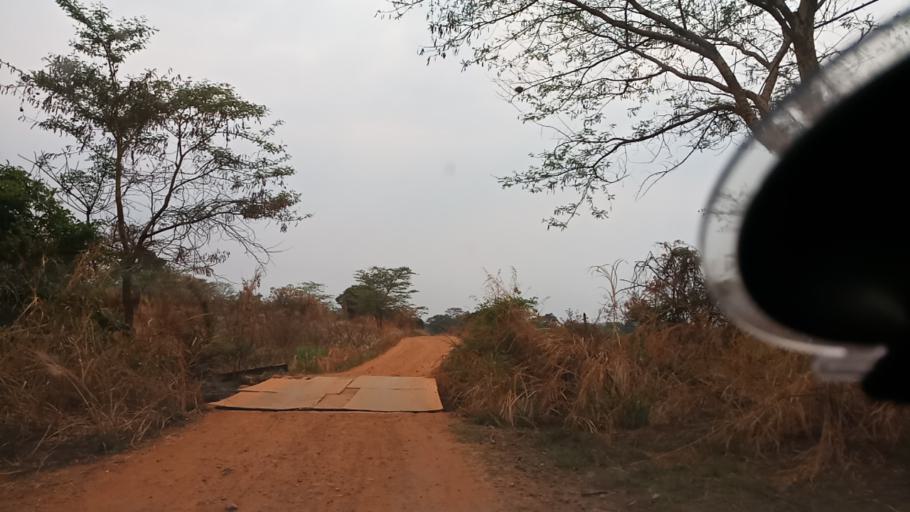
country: ZM
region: Luapula
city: Nchelenge
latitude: -9.0942
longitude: 28.3259
